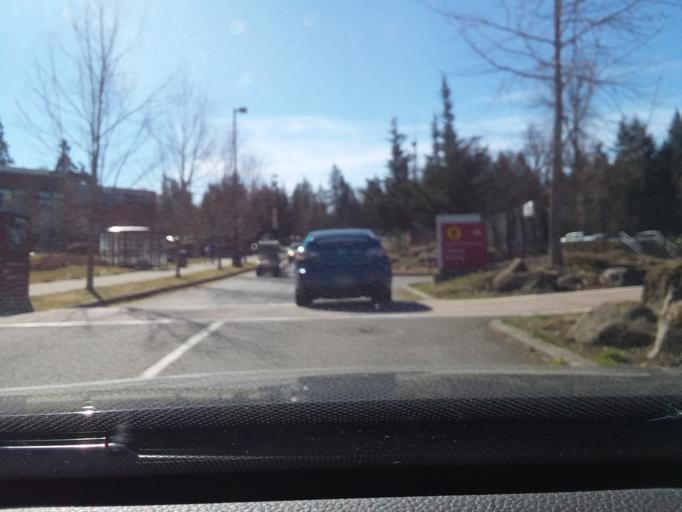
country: US
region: Washington
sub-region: Pierce County
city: South Hill
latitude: 47.1580
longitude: -122.2740
